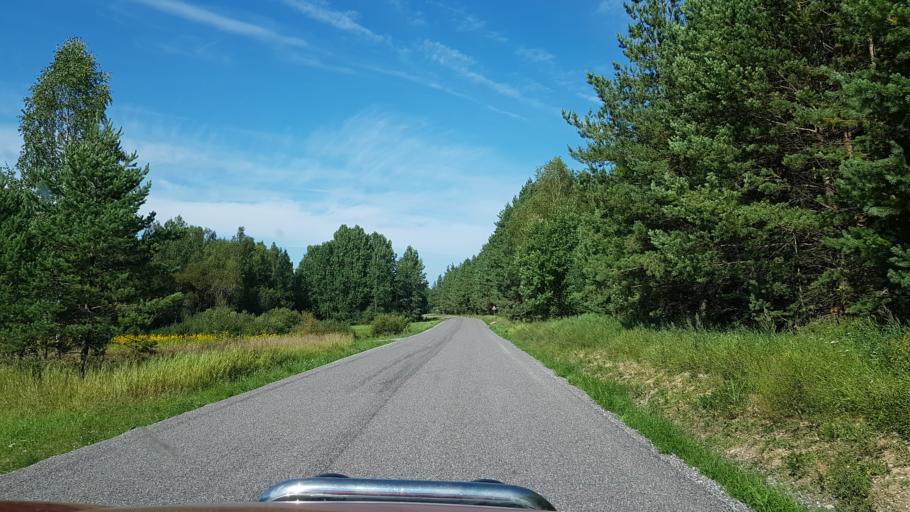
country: EE
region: Tartu
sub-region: Elva linn
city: Elva
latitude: 58.2479
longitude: 26.3785
